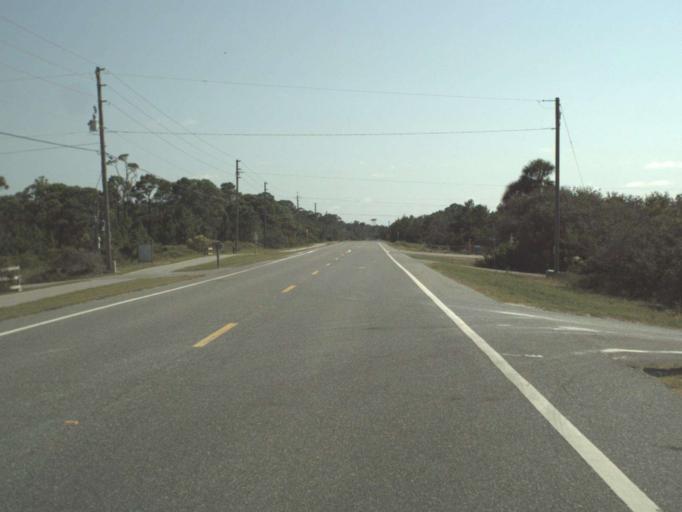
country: US
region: Florida
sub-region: Gulf County
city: Port Saint Joe
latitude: 29.7180
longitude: -85.3848
